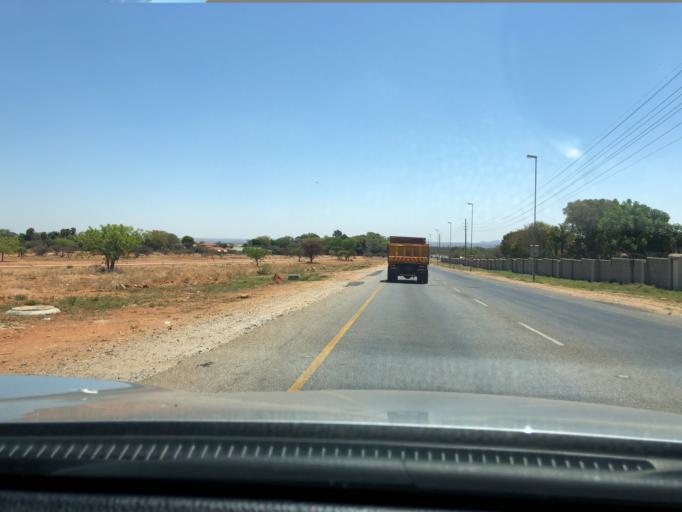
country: ZA
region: Limpopo
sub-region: Capricorn District Municipality
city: Polokwane
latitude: -23.8808
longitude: 29.4969
